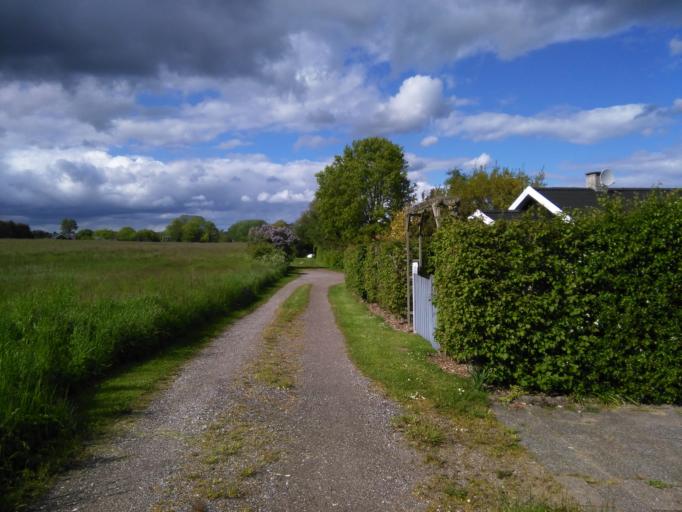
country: DK
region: Central Jutland
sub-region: Arhus Kommune
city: Beder
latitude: 56.0362
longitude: 10.2633
